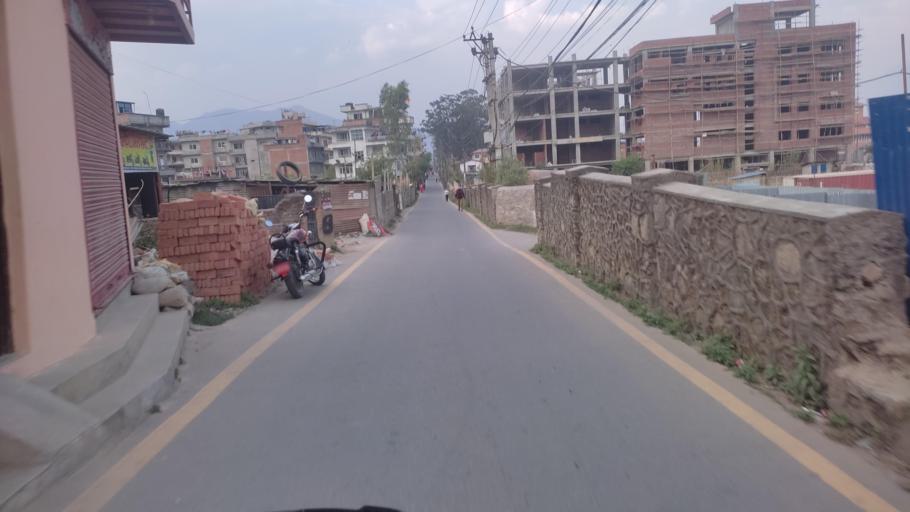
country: NP
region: Central Region
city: Kirtipur
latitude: 27.6779
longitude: 85.2817
